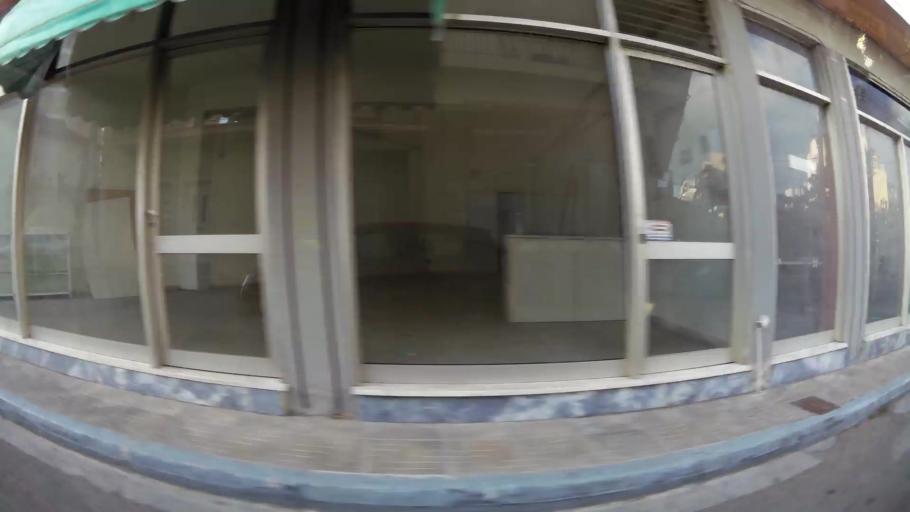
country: GR
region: Attica
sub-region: Nomarchia Anatolikis Attikis
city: Acharnes
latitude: 38.0764
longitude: 23.7406
